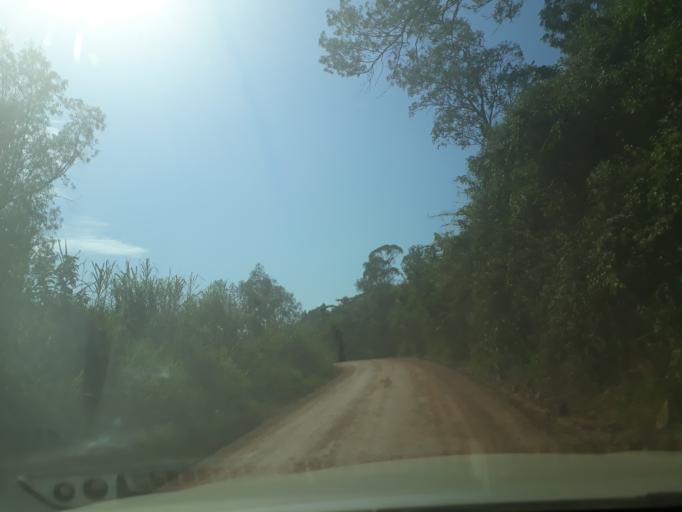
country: CD
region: Eastern Province
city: Bunia
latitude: 1.8117
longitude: 30.4208
